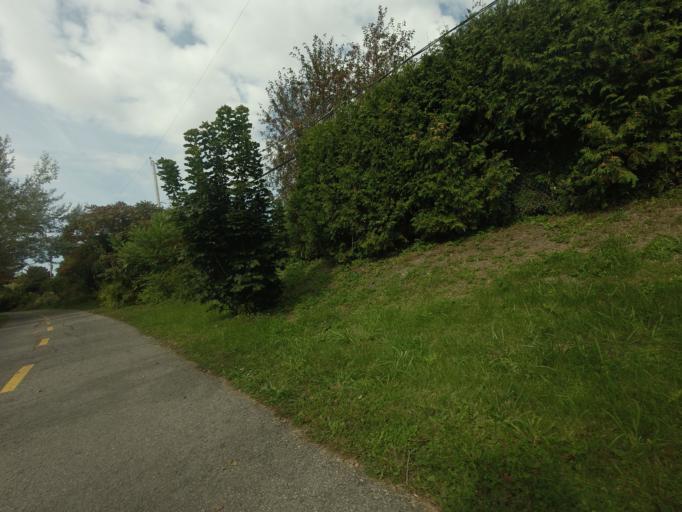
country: CA
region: Quebec
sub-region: Laurentides
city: Blainville
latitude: 45.6896
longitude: -73.8881
